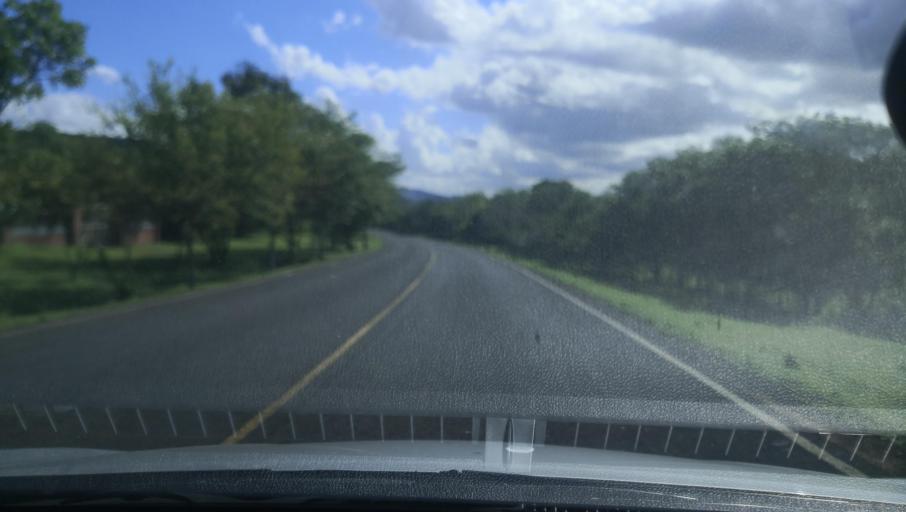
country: NI
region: Madriz
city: Somoto
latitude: 13.4720
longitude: -86.6210
